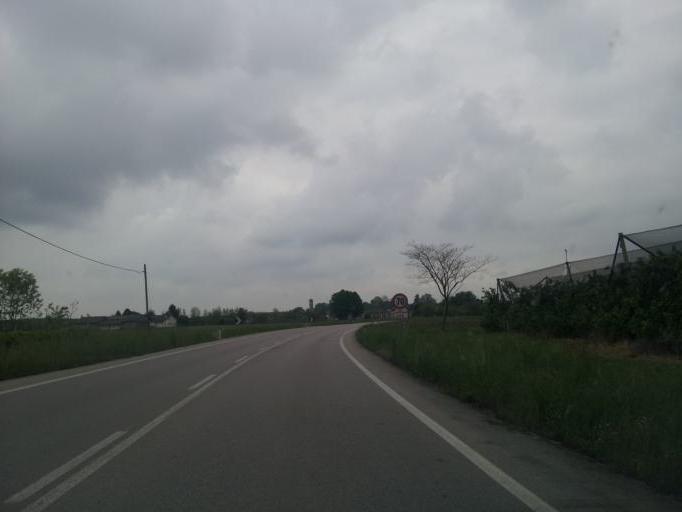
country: IT
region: Friuli Venezia Giulia
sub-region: Provincia di Udine
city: Varmo
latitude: 45.9144
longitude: 12.9977
